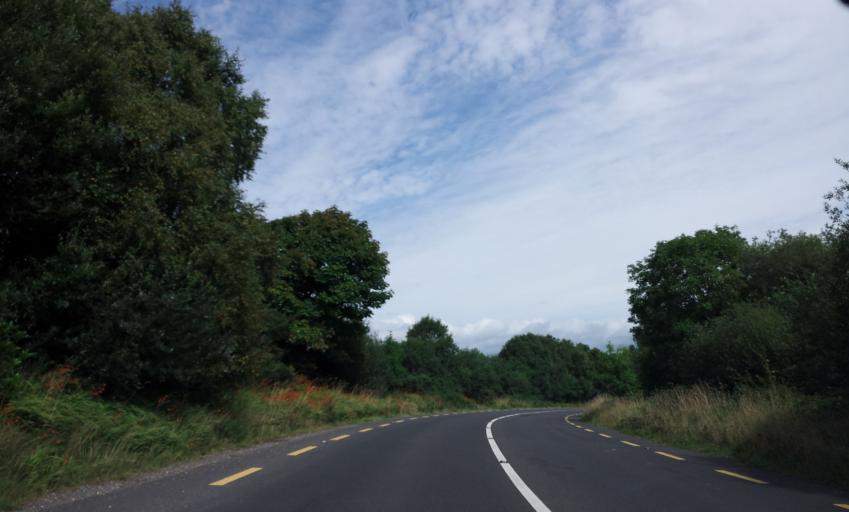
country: IE
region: Munster
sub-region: Ciarrai
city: Killorglin
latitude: 52.1029
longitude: -9.8239
